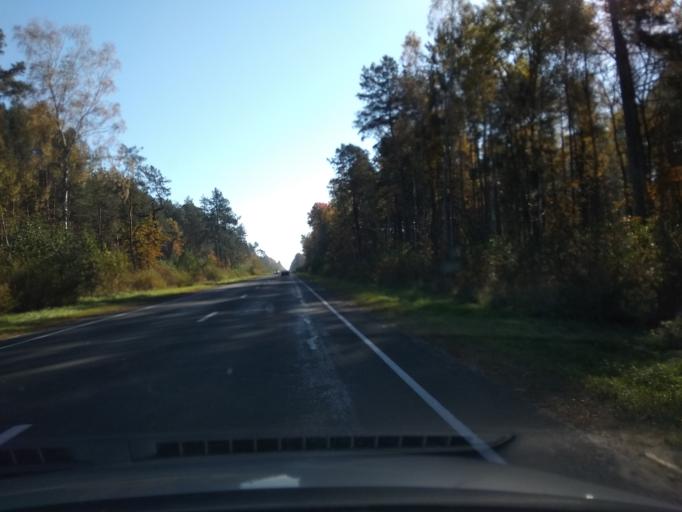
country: BY
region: Brest
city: Malaryta
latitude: 51.9109
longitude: 24.1021
